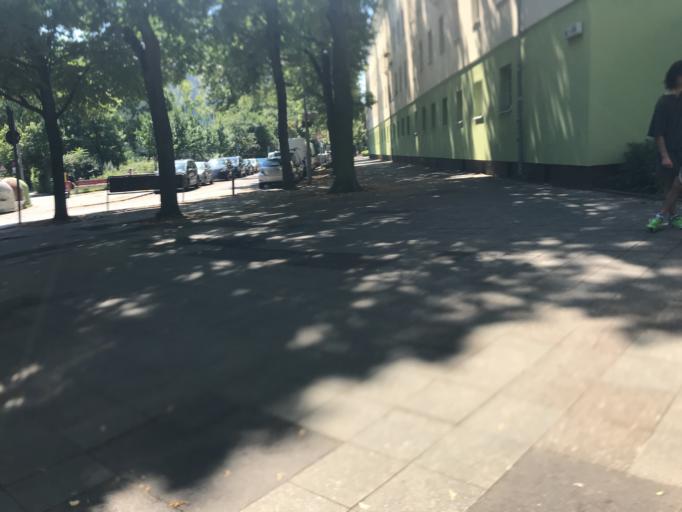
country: DE
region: Berlin
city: Plaenterwald
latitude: 52.4736
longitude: 13.4644
